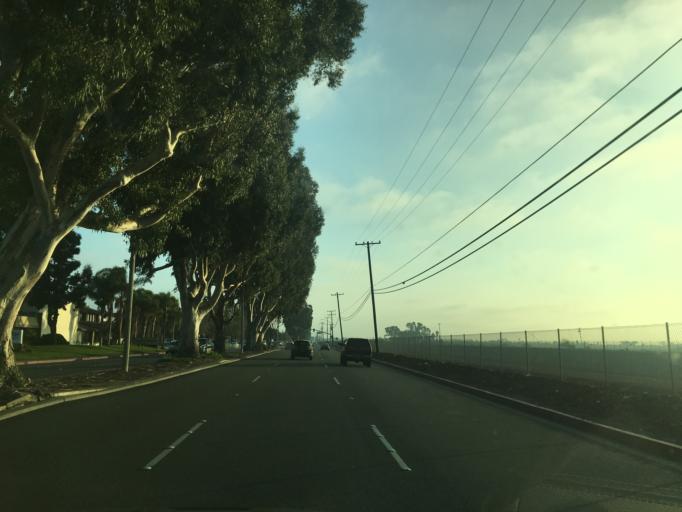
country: US
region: California
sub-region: Orange County
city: Westminster
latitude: 33.7433
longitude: -118.0419
